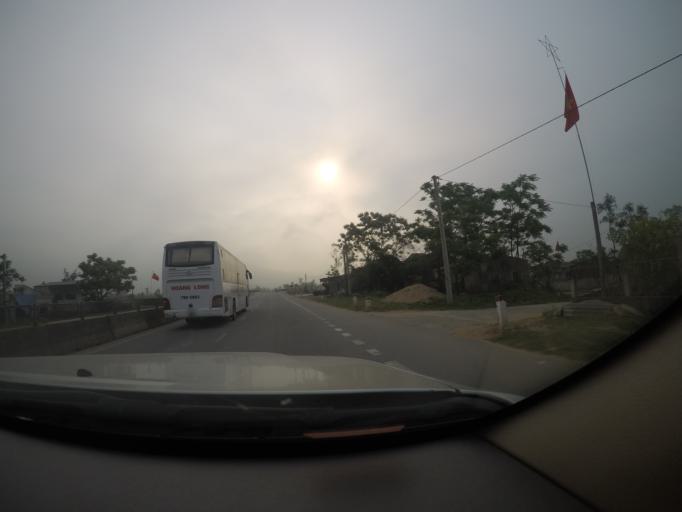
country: VN
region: Ha Tinh
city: Cam Xuyen
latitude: 18.2112
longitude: 106.1122
